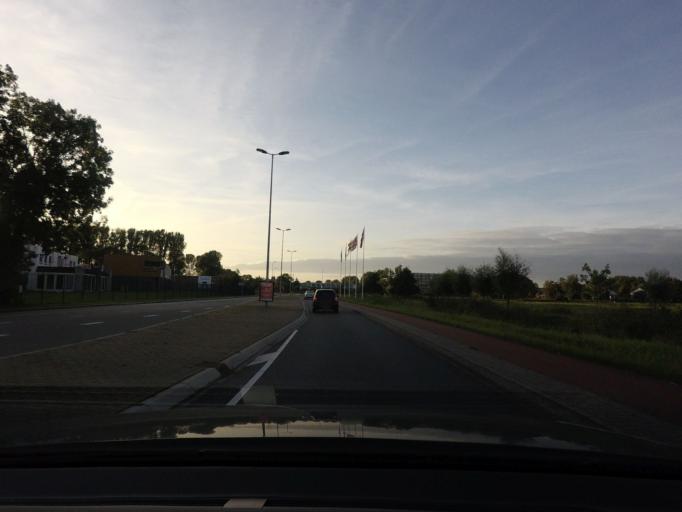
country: NL
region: North Holland
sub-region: Gemeente Alkmaar
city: Alkmaar
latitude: 52.6275
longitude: 4.7716
